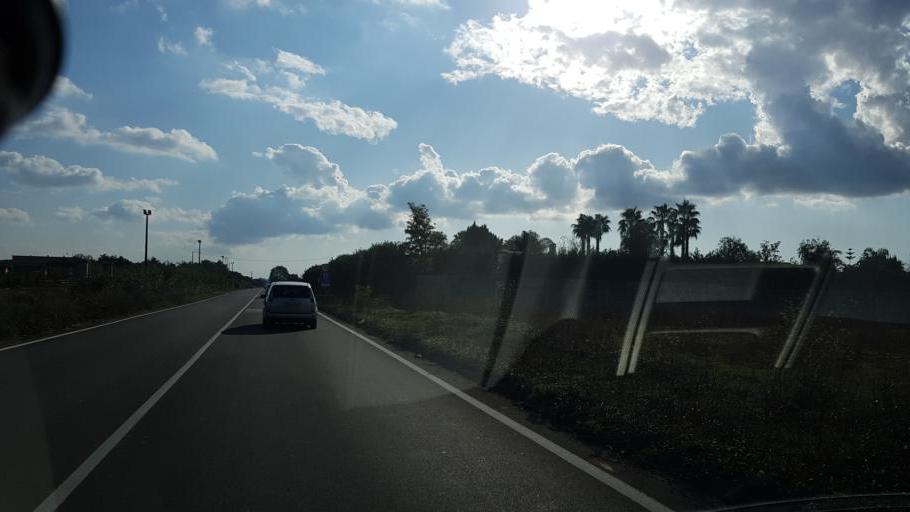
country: IT
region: Apulia
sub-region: Provincia di Lecce
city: Salice Salentino
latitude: 40.3649
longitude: 17.9674
